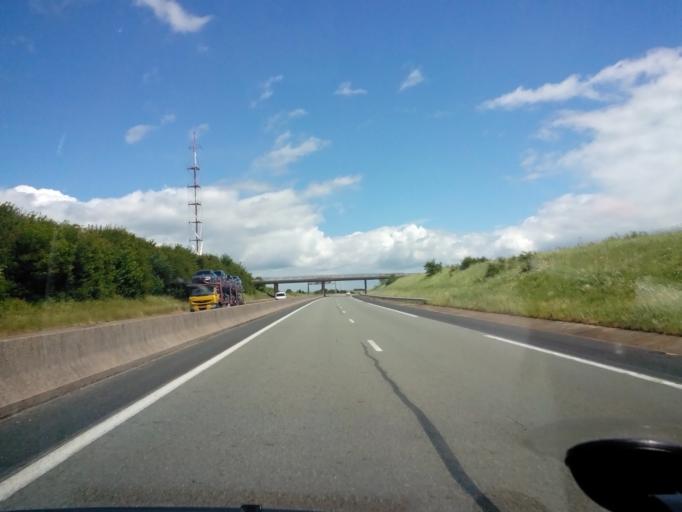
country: FR
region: Lorraine
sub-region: Departement des Vosges
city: Bulgneville
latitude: 48.1745
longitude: 5.7263
